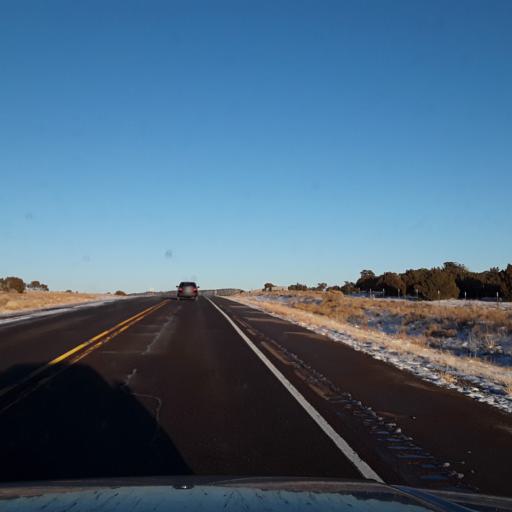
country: US
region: New Mexico
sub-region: Lincoln County
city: Carrizozo
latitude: 34.2346
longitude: -105.6174
